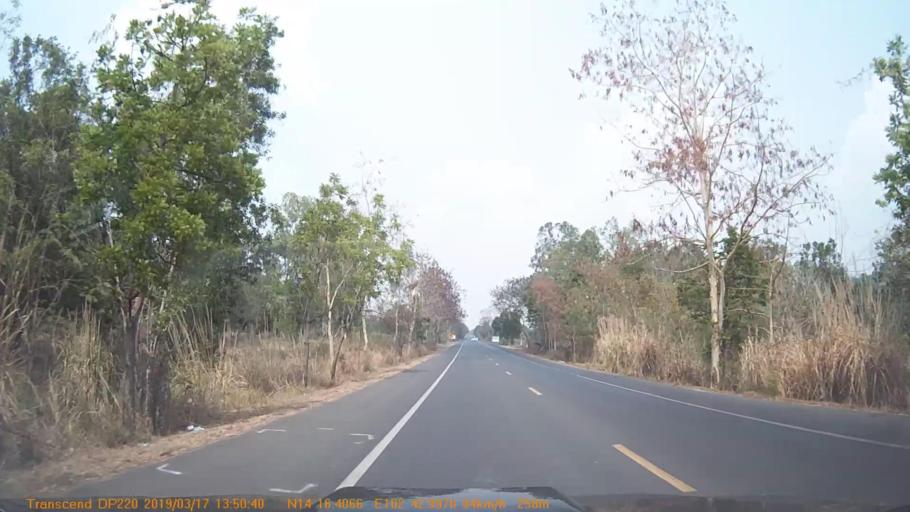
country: TH
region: Buriram
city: Non Din Daeng
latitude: 14.2738
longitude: 102.7170
